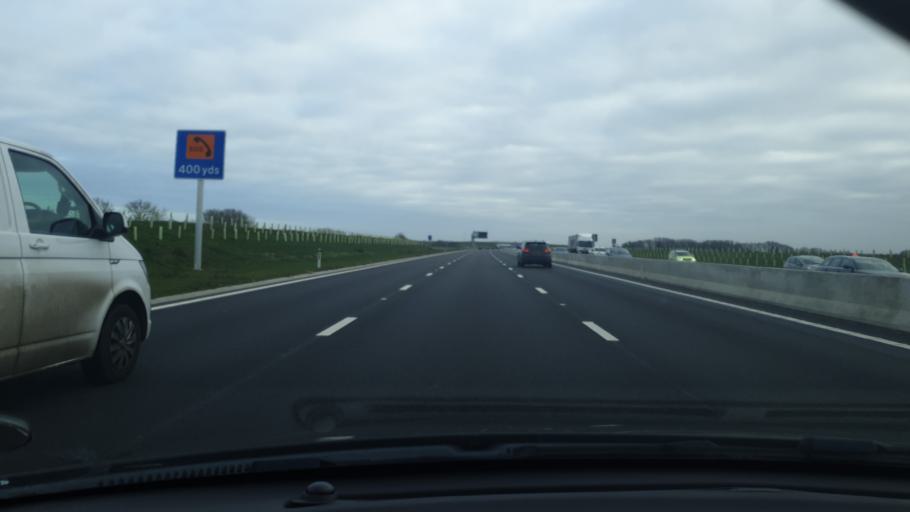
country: GB
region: England
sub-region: Cambridgeshire
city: Hemingford Grey
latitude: 52.2927
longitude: -0.1149
